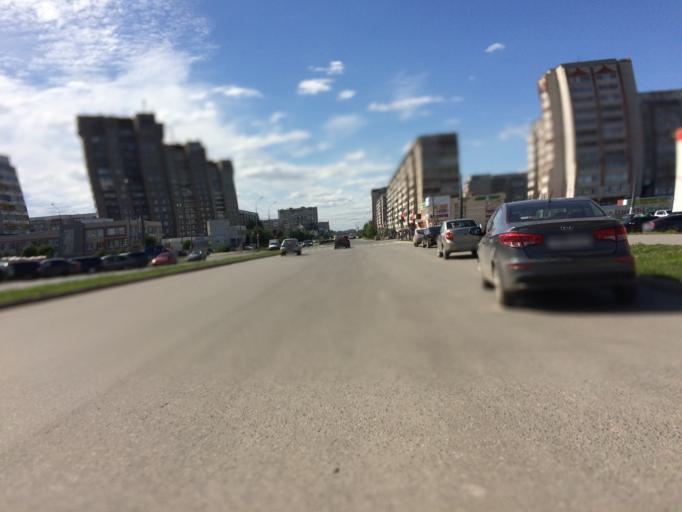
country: RU
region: Mariy-El
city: Yoshkar-Ola
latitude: 56.6335
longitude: 47.9331
